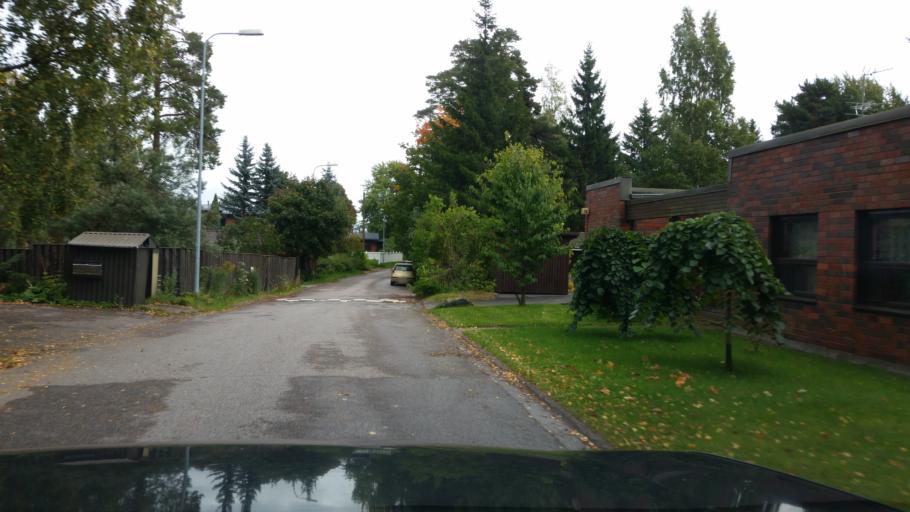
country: FI
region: Uusimaa
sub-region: Helsinki
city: Helsinki
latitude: 60.2365
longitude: 24.9654
